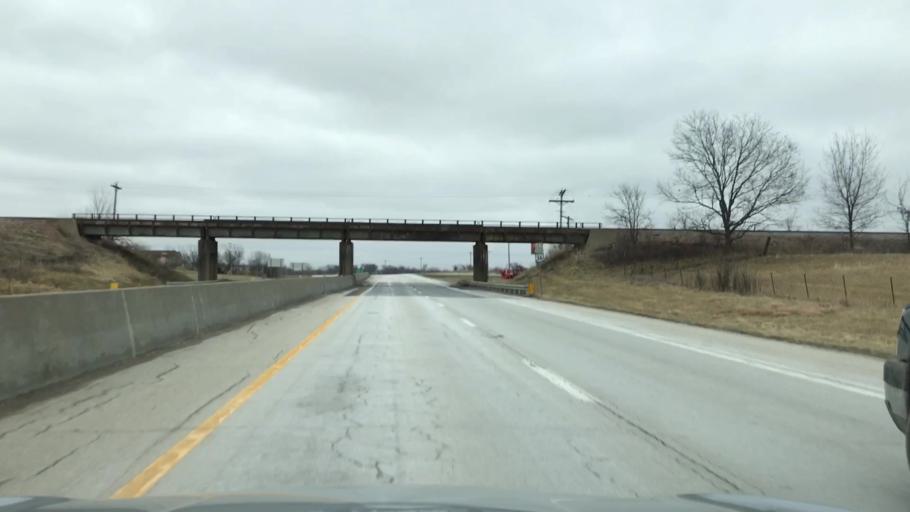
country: US
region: Missouri
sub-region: Livingston County
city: Chillicothe
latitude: 39.7732
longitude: -93.5427
